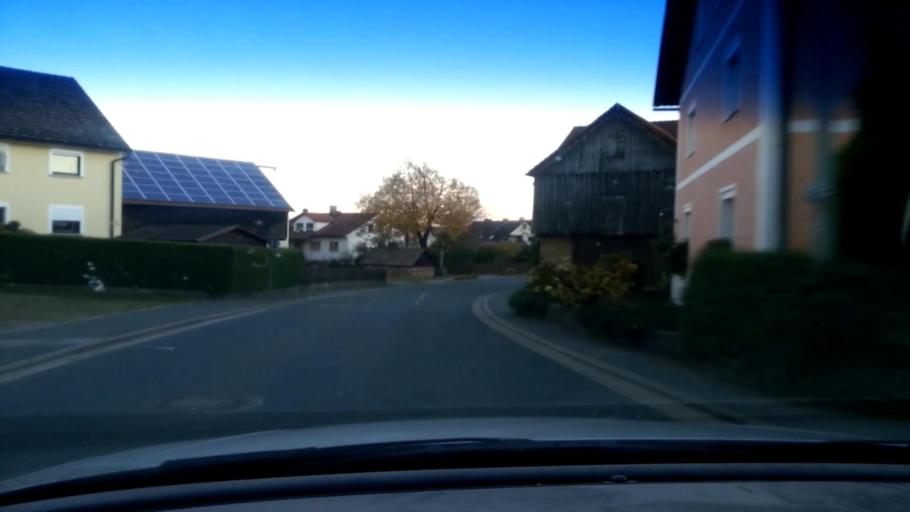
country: DE
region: Bavaria
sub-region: Upper Franconia
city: Poxdorf
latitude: 49.8740
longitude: 11.0923
